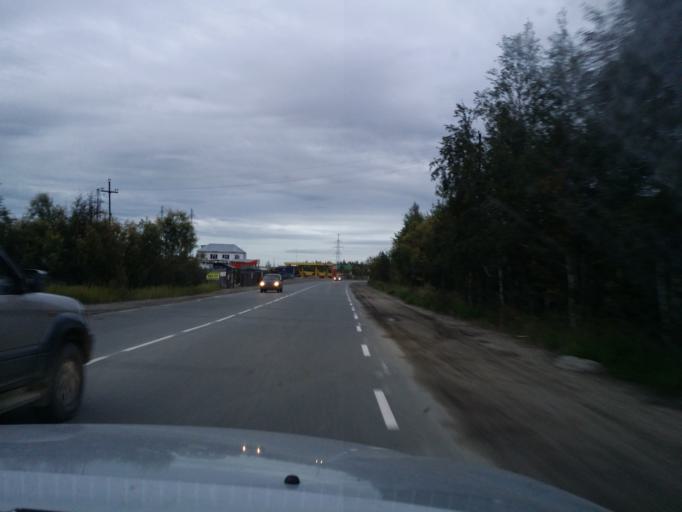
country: RU
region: Khanty-Mansiyskiy Avtonomnyy Okrug
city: Nizhnevartovsk
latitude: 60.9653
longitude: 76.6587
